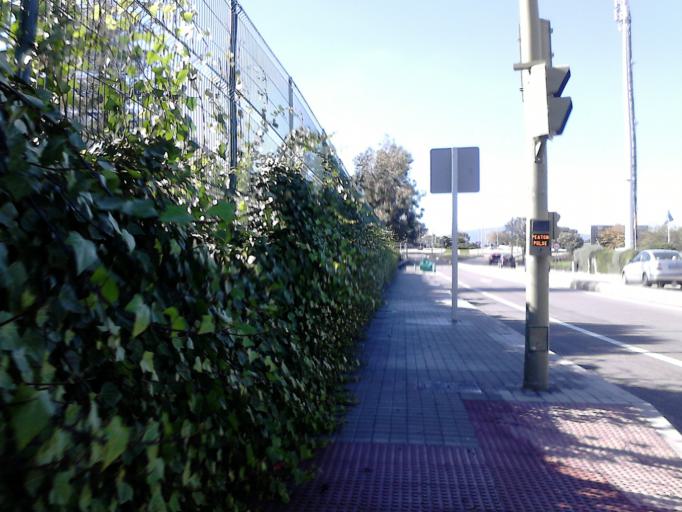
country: ES
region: Madrid
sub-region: Provincia de Madrid
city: Galapagar
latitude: 40.5715
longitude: -3.9962
